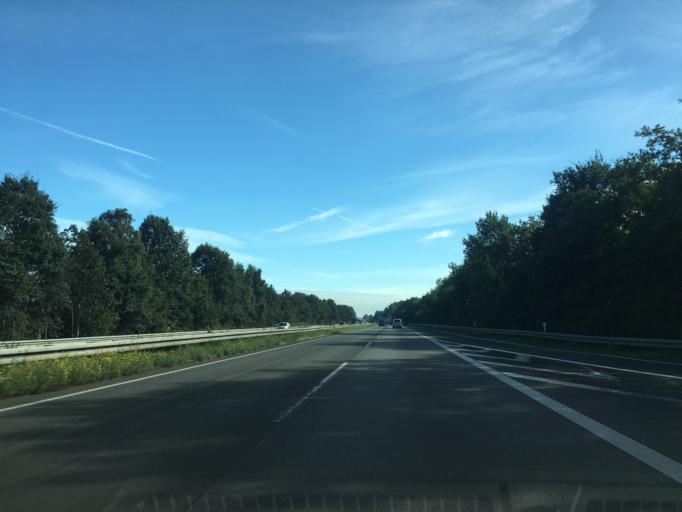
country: DE
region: North Rhine-Westphalia
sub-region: Regierungsbezirk Munster
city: Ladbergen
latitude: 52.1007
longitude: 7.6771
